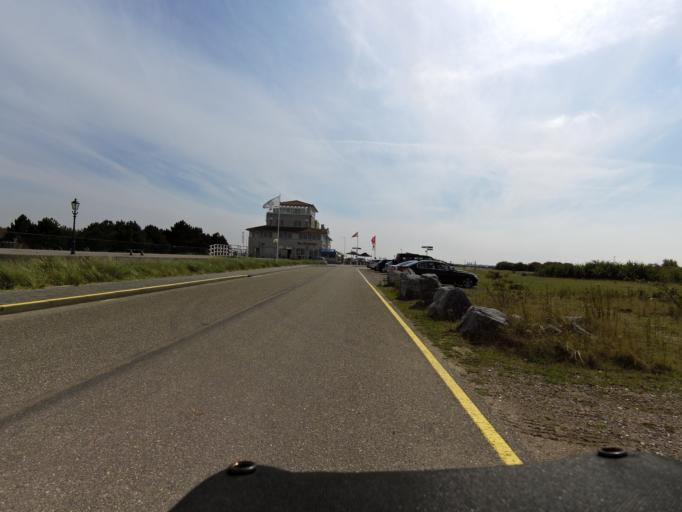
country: NL
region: Zeeland
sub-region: Schouwen-Duiveland
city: Scharendijke
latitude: 51.7583
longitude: 3.8543
